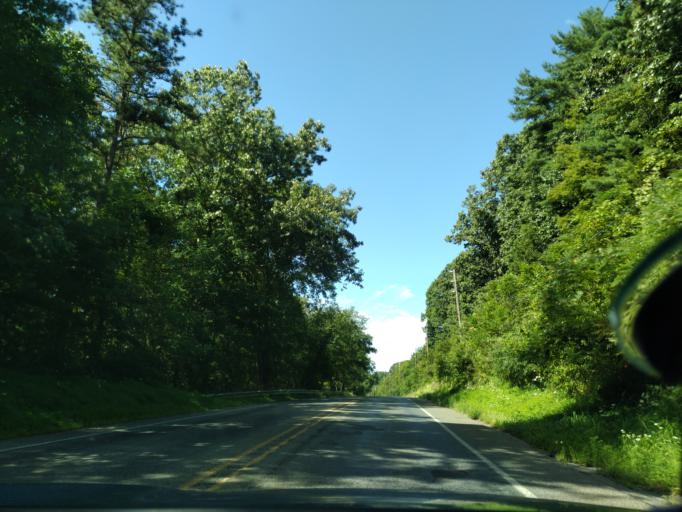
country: US
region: Pennsylvania
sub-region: Pike County
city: Saw Creek
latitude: 41.0995
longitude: -74.9930
